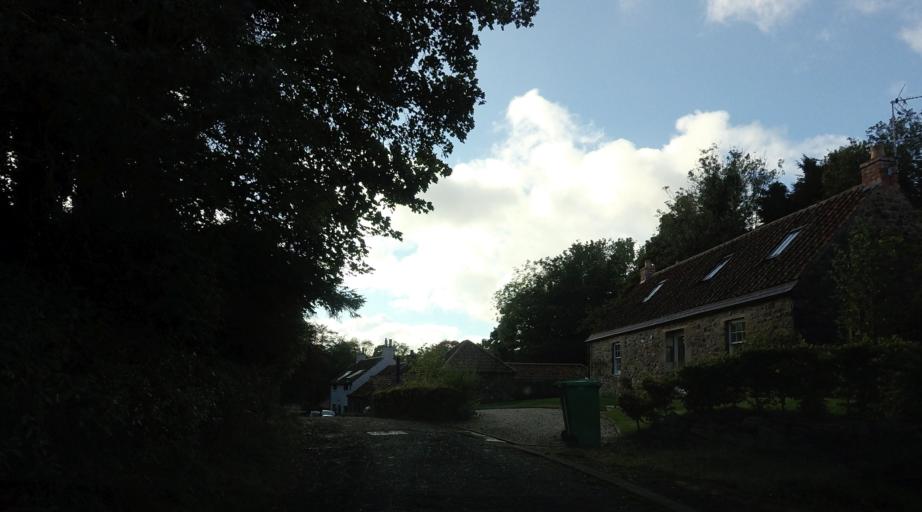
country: GB
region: Scotland
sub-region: Fife
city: Balmullo
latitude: 56.3845
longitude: -2.9926
